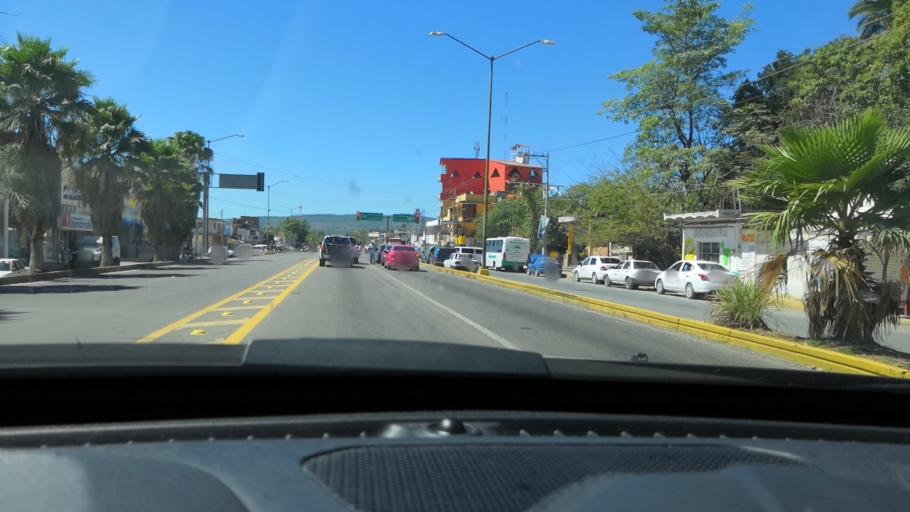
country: MX
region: Nayarit
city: Las Varas
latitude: 21.1800
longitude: -105.1357
